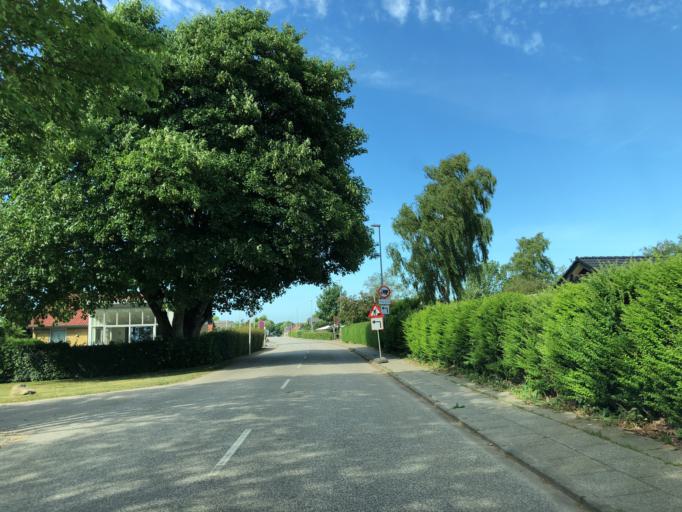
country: DK
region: Central Jutland
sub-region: Herning Kommune
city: Snejbjerg
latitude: 56.1273
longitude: 8.8879
